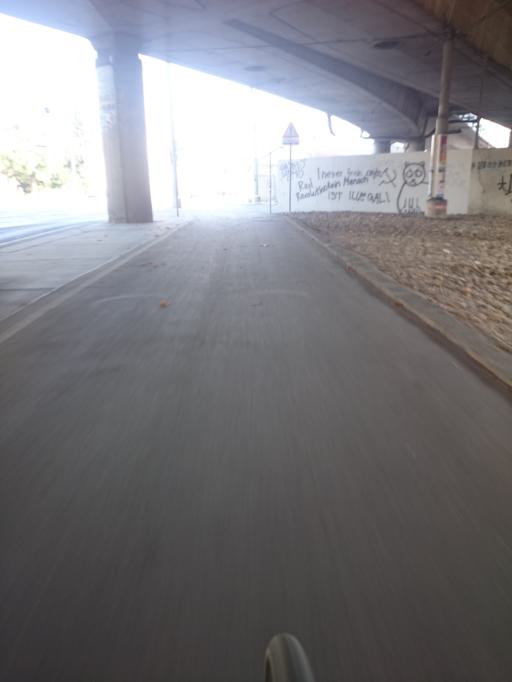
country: AT
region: Lower Austria
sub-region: Politischer Bezirk Korneuburg
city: Langenzersdorf
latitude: 48.2626
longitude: 16.3950
